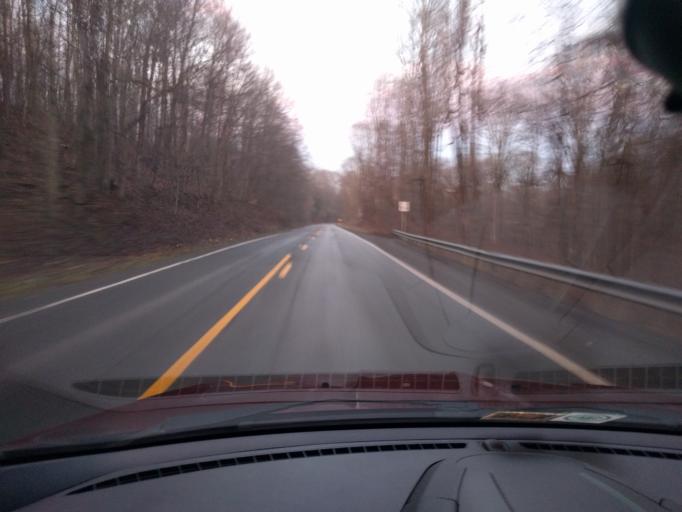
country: US
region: West Virginia
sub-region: Greenbrier County
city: Rainelle
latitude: 38.0117
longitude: -80.8864
